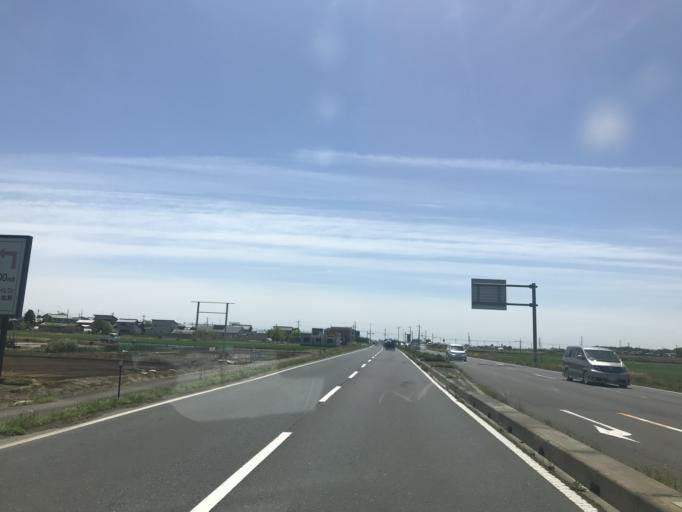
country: JP
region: Ibaraki
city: Ishige
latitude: 36.2051
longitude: 139.9844
